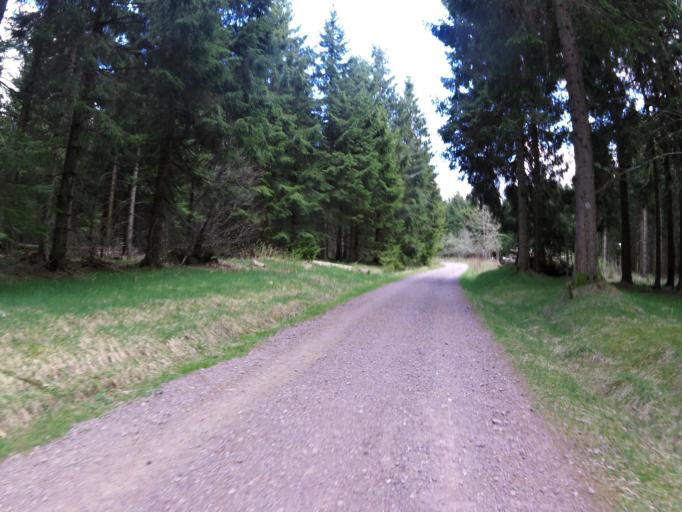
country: DE
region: Thuringia
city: Oberhof
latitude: 50.7072
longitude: 10.6840
